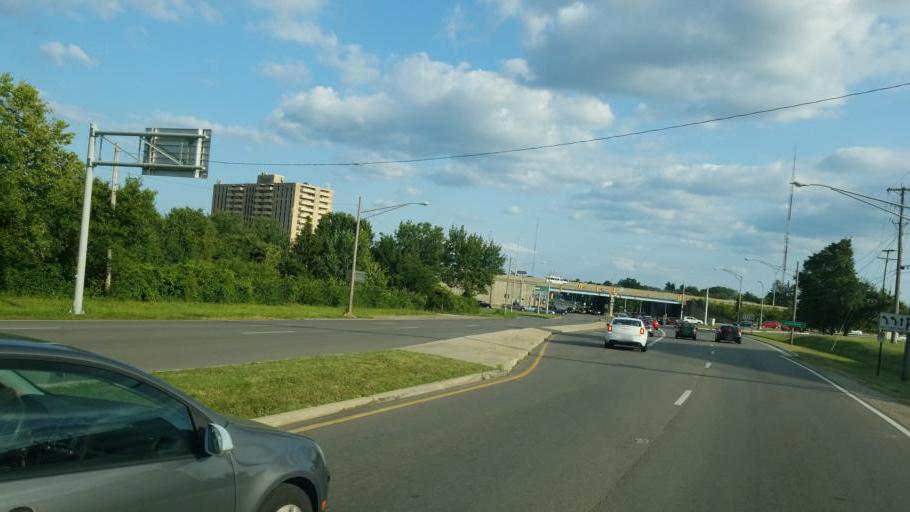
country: US
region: Ohio
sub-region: Franklin County
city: Upper Arlington
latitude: 40.0320
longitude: -83.0314
